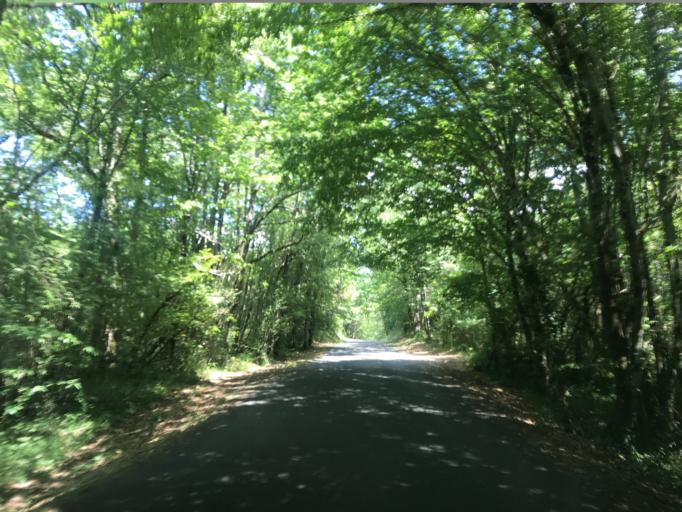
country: FR
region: Aquitaine
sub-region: Departement de la Dordogne
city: Cenac-et-Saint-Julien
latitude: 44.8382
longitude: 1.1958
